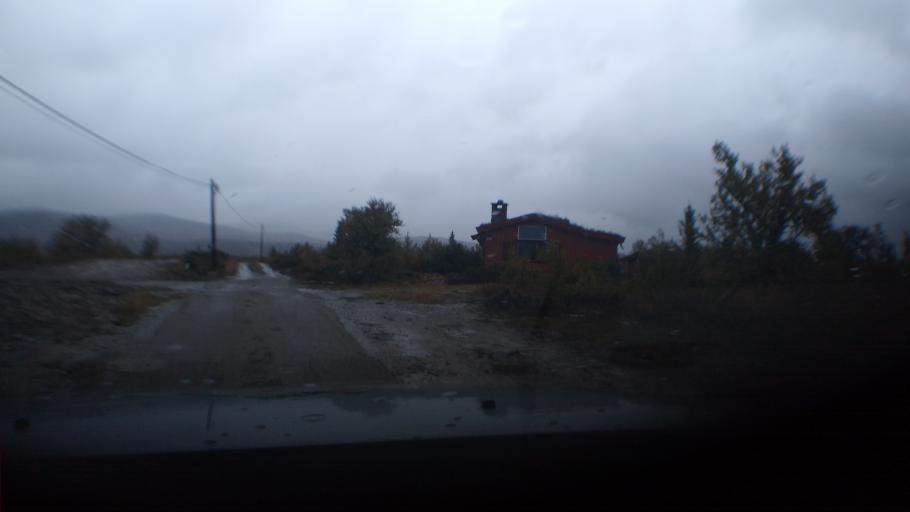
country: NO
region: Oppland
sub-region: Ringebu
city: Ringebu
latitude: 61.6606
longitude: 10.1040
